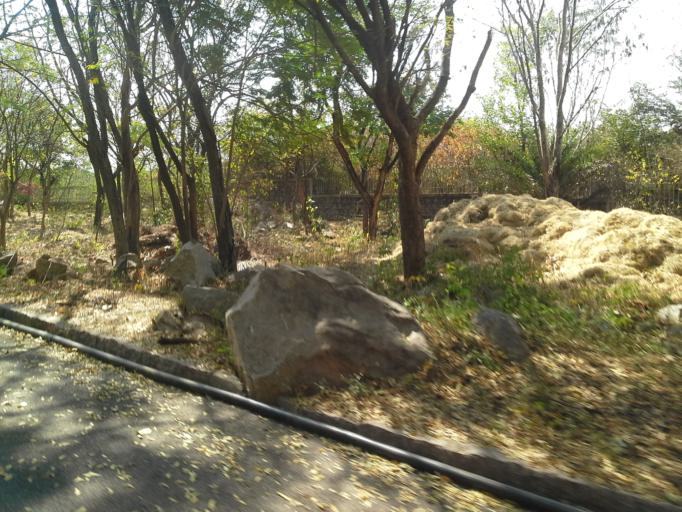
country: IN
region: Telangana
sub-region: Hyderabad
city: Hyderabad
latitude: 17.3106
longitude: 78.4094
